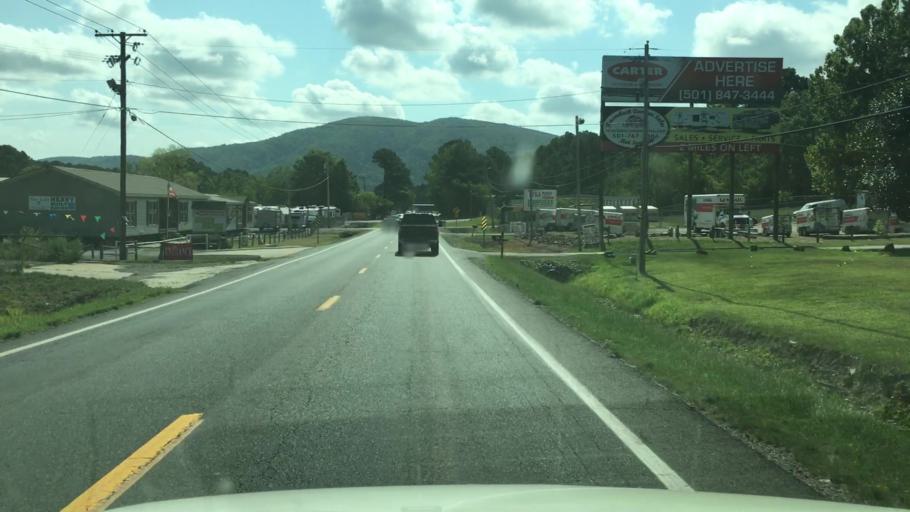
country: US
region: Arkansas
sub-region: Garland County
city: Piney
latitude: 34.5078
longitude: -93.1356
